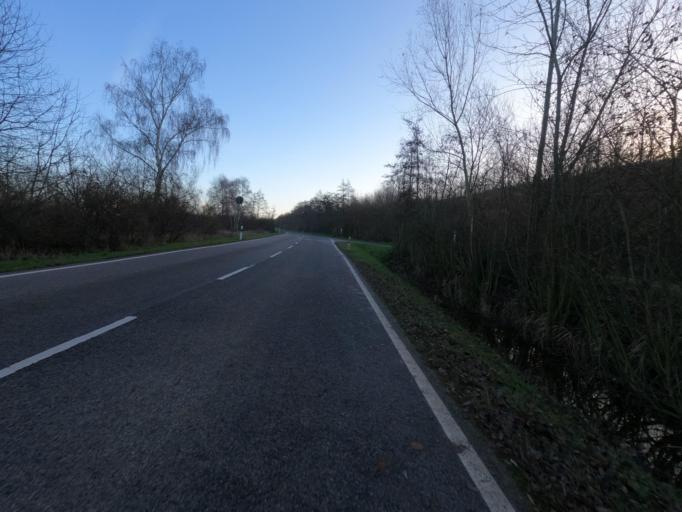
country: DE
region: North Rhine-Westphalia
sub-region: Regierungsbezirk Koln
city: Niederzier
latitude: 50.9358
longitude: 6.4972
